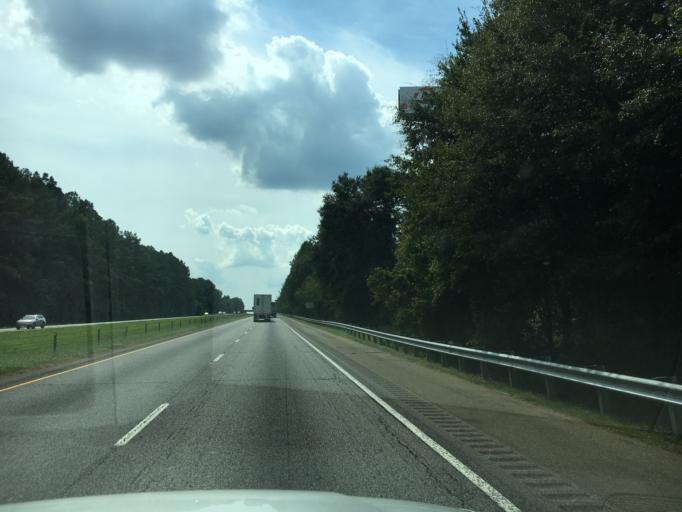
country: US
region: Georgia
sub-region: Franklin County
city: Carnesville
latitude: 34.3690
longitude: -83.2773
